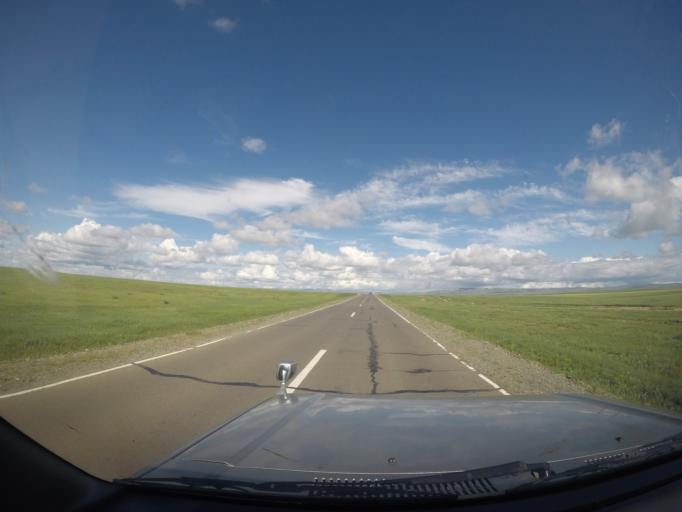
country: MN
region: Hentiy
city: Moron
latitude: 47.4181
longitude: 109.9259
